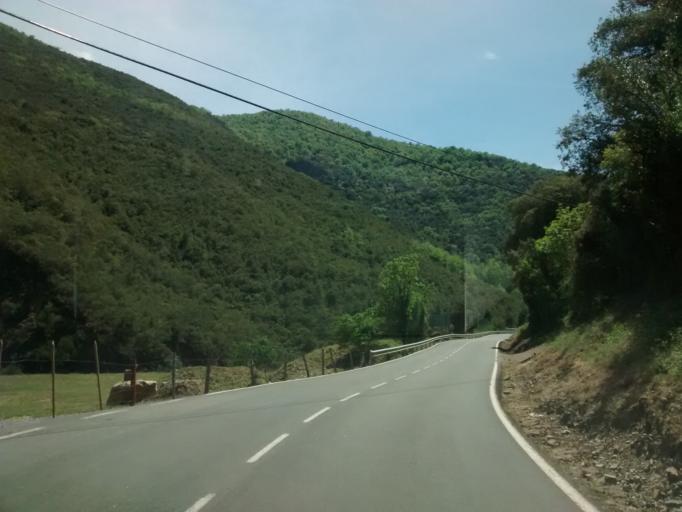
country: ES
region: Cantabria
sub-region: Provincia de Cantabria
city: Potes
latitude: 43.1078
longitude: -4.6417
